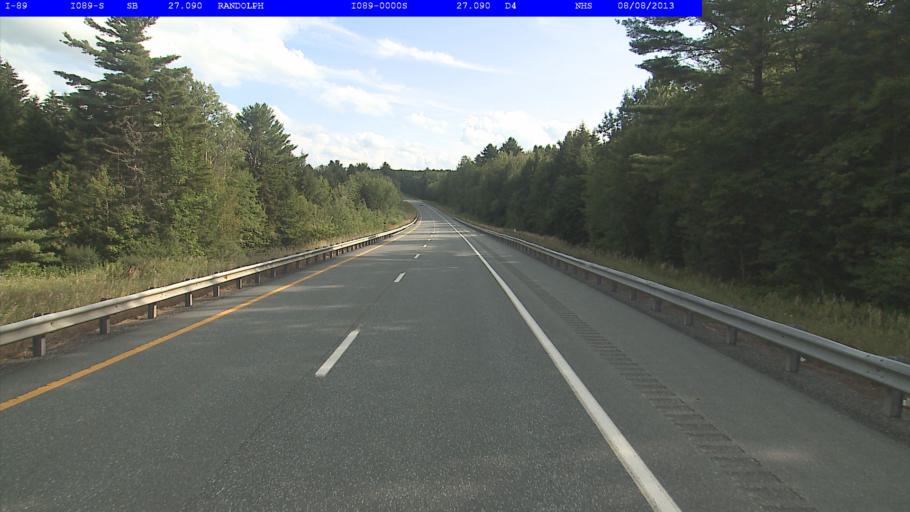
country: US
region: Vermont
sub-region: Orange County
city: Randolph
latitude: 43.8913
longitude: -72.6175
